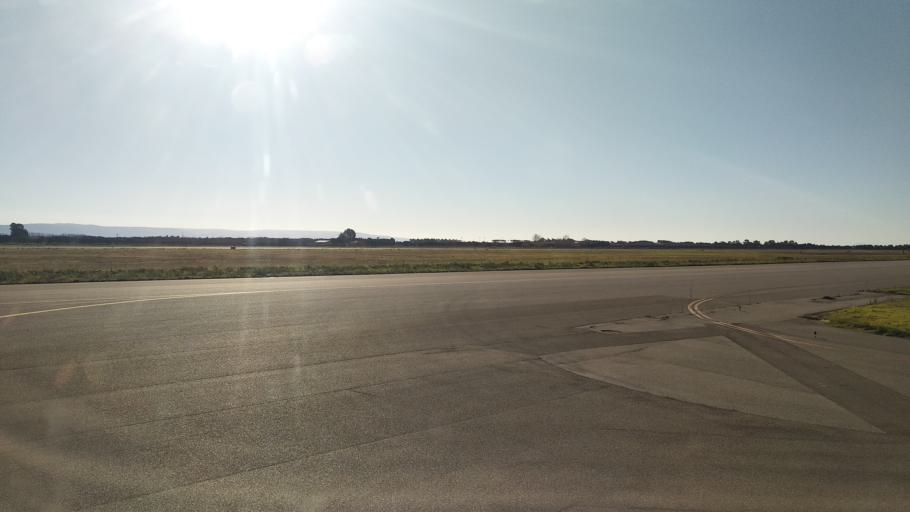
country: IT
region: Calabria
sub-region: Provincia di Catanzaro
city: Santa Eufemia Lamezia
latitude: 38.9076
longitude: 16.2458
